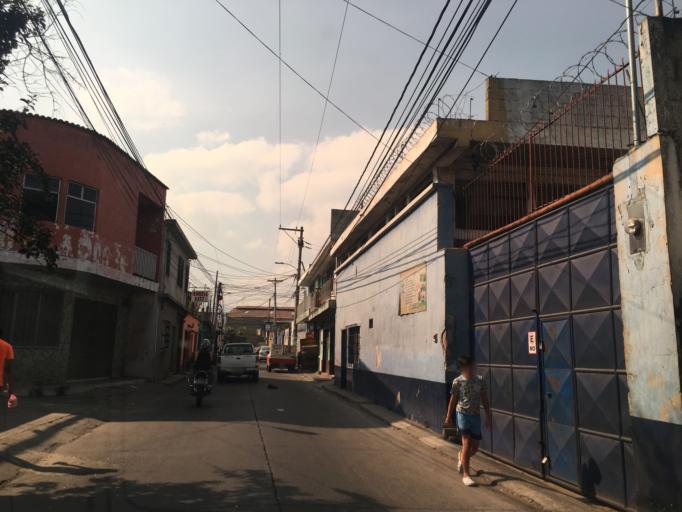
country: GT
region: Guatemala
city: Villa Nueva
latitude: 14.5279
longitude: -90.5862
